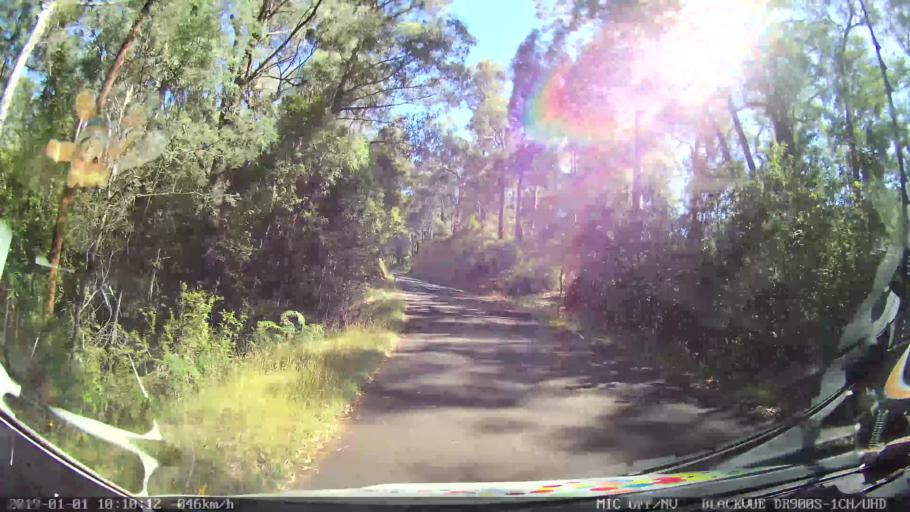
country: AU
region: New South Wales
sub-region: Snowy River
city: Jindabyne
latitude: -36.1429
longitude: 148.1584
